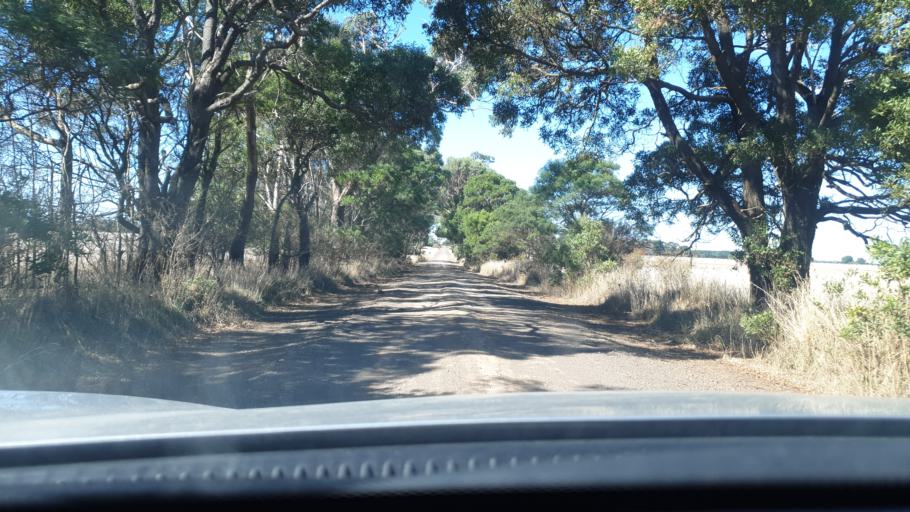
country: AU
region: Victoria
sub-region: Warrnambool
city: Warrnambool
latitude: -38.1648
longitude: 142.3891
